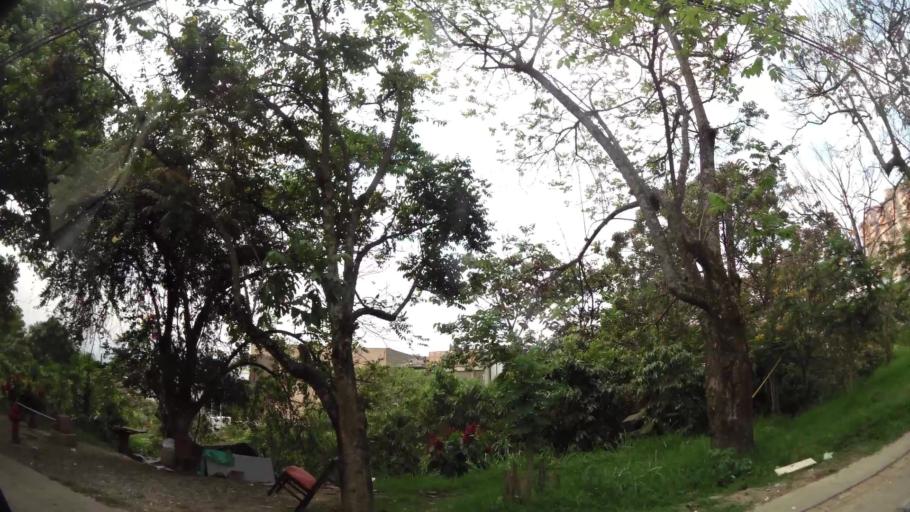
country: CO
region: Antioquia
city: Itagui
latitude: 6.1899
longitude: -75.6011
